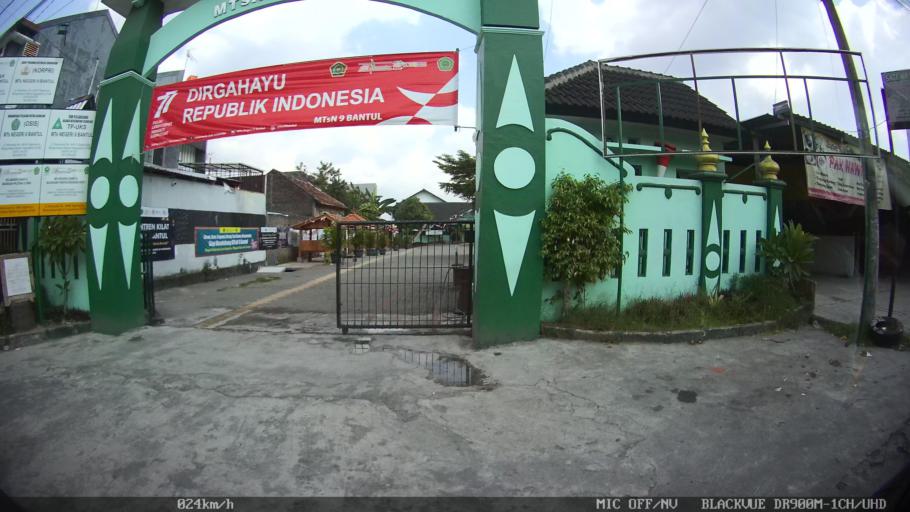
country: ID
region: Daerah Istimewa Yogyakarta
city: Depok
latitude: -7.8026
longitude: 110.4081
